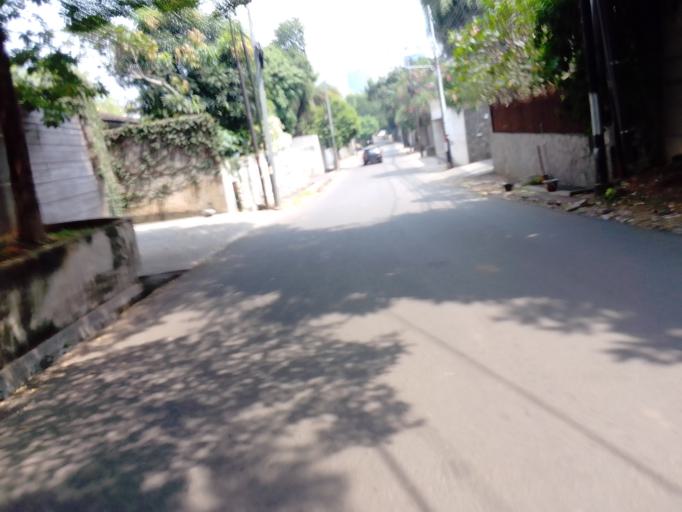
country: ID
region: Jakarta Raya
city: Jakarta
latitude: -6.2300
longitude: 106.8136
